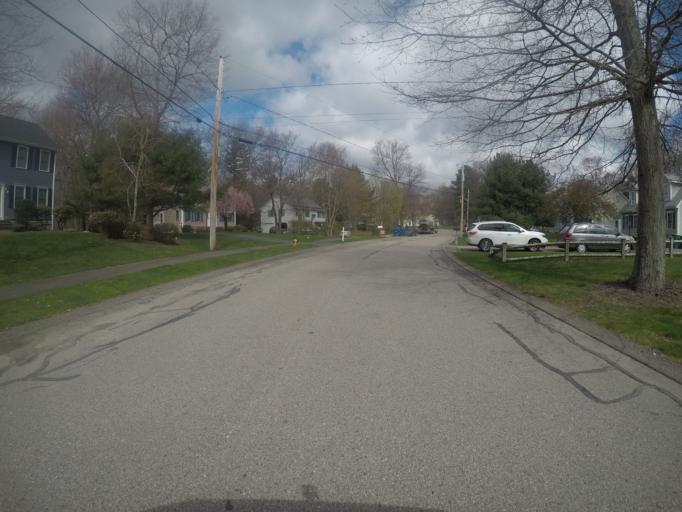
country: US
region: Massachusetts
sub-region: Bristol County
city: Easton
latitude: 42.0291
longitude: -71.1596
